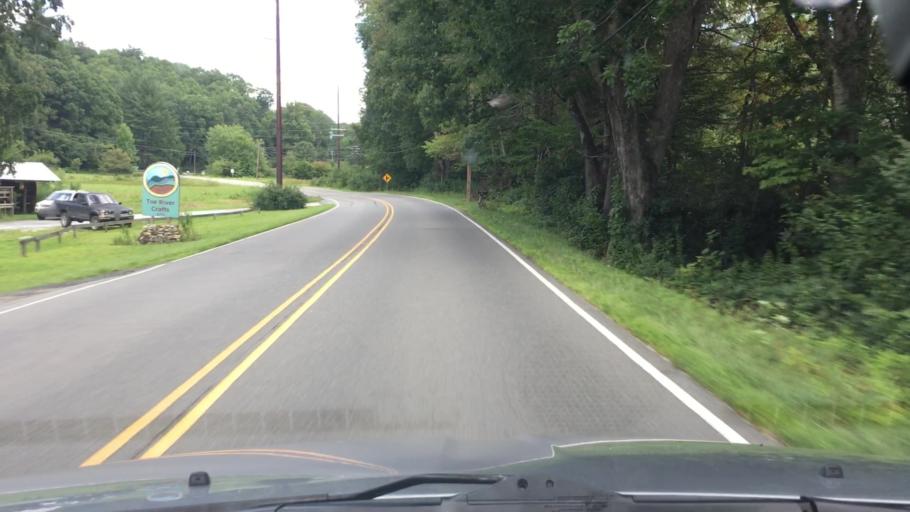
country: US
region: North Carolina
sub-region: Yancey County
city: Burnsville
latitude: 35.8305
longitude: -82.1851
